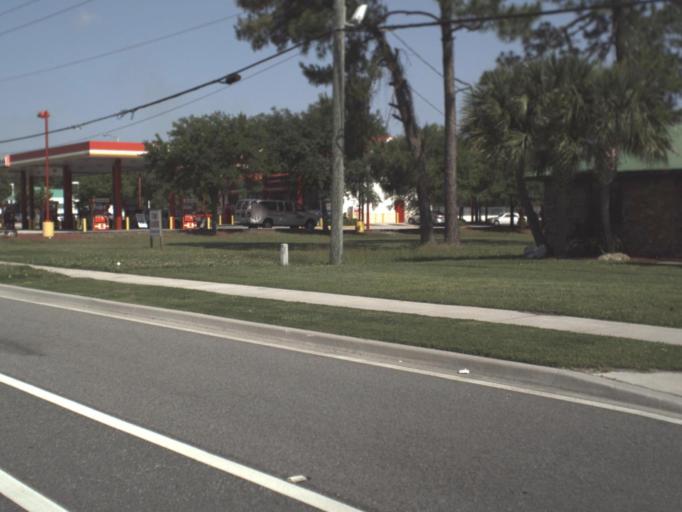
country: US
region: Florida
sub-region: Duval County
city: Jacksonville Beach
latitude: 30.2878
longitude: -81.4575
